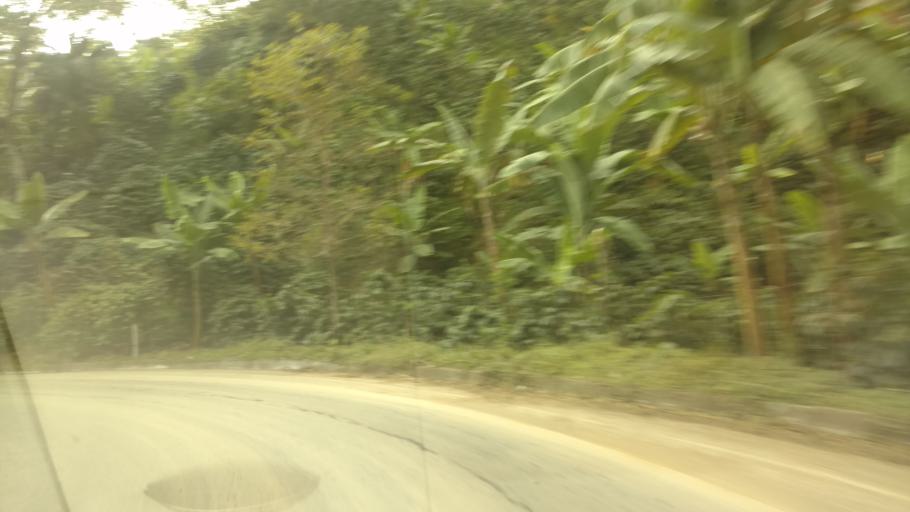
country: CO
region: Caldas
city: Neira
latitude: 5.1873
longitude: -75.5423
